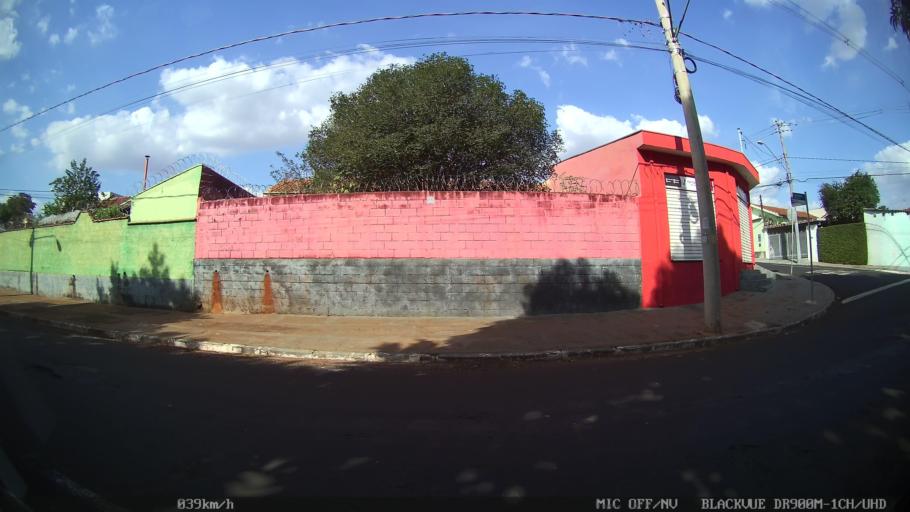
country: BR
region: Sao Paulo
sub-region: Ribeirao Preto
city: Ribeirao Preto
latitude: -21.1855
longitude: -47.8428
